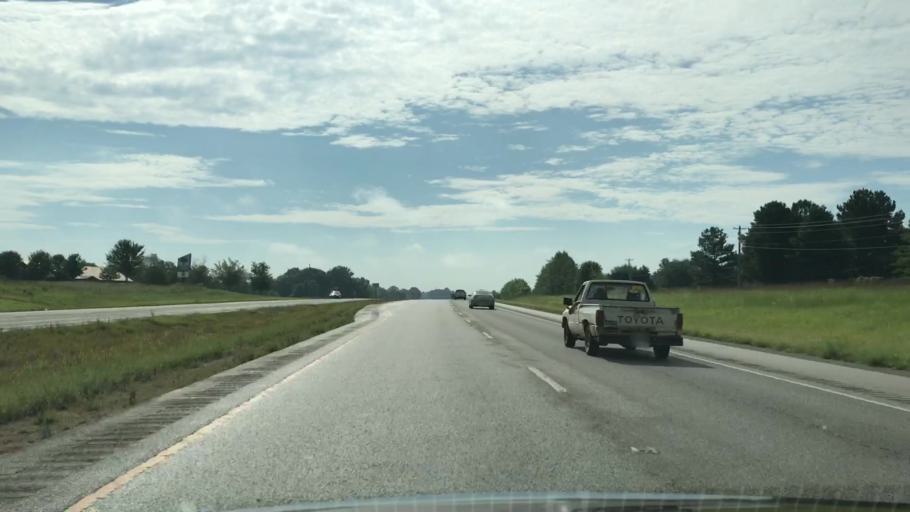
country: US
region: Kentucky
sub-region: Warren County
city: Plano
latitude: 36.8874
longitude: -86.3686
